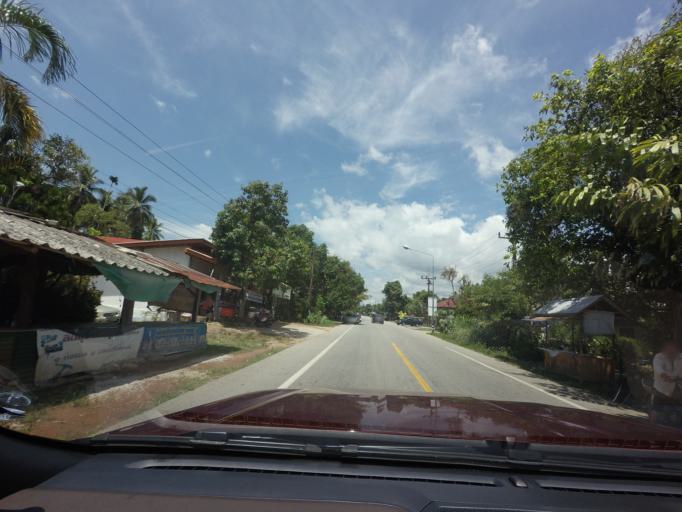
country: TH
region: Narathiwat
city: Ra-ngae
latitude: 6.2332
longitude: 101.6764
